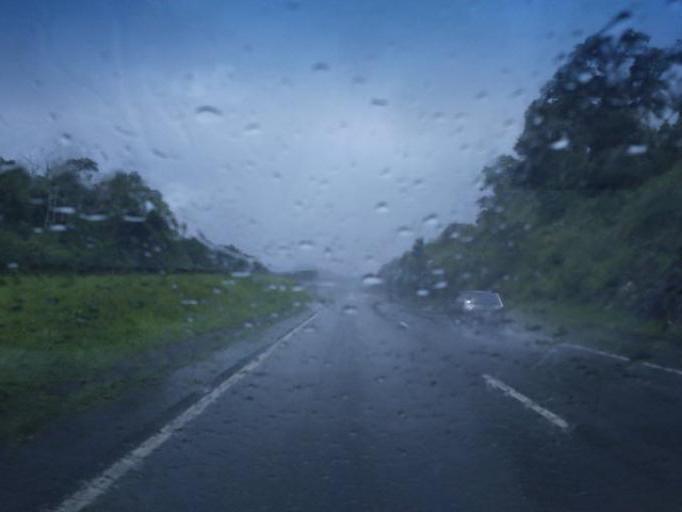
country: BR
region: Sao Paulo
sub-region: Cajati
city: Cajati
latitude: -24.9707
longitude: -48.3782
